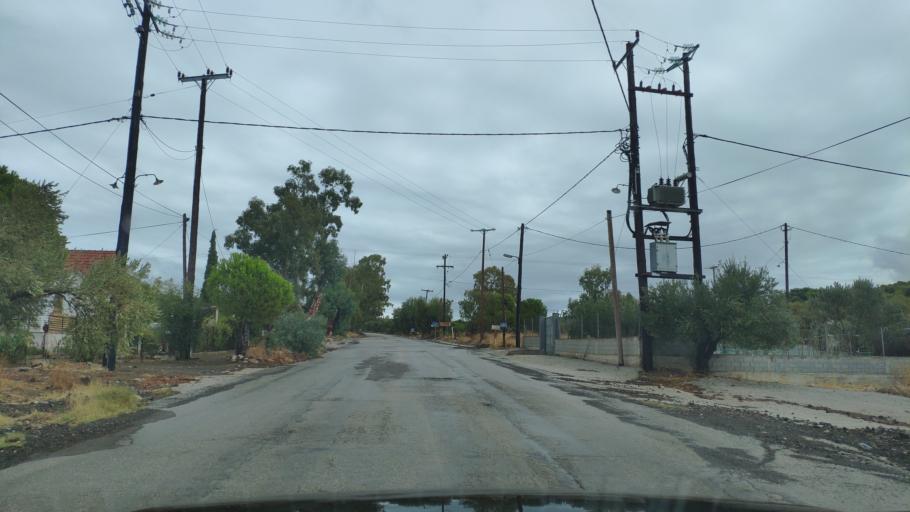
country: GR
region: Peloponnese
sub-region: Nomos Korinthias
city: Loutraki
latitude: 37.9647
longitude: 22.9995
